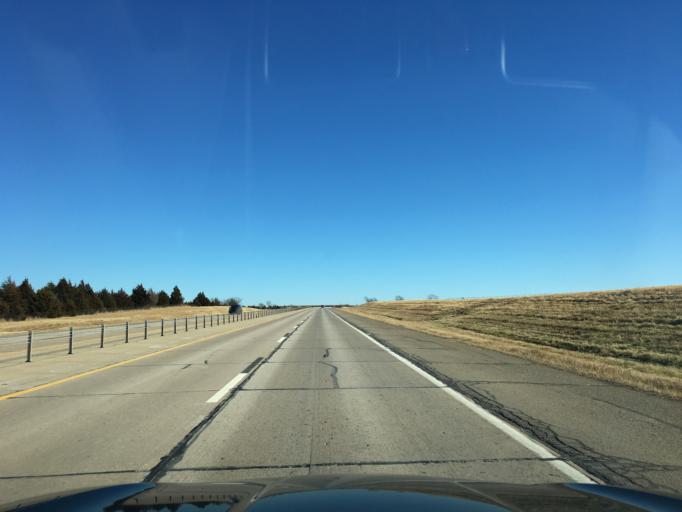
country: US
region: Oklahoma
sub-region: Pawnee County
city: Pawnee
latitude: 36.2250
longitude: -96.8464
